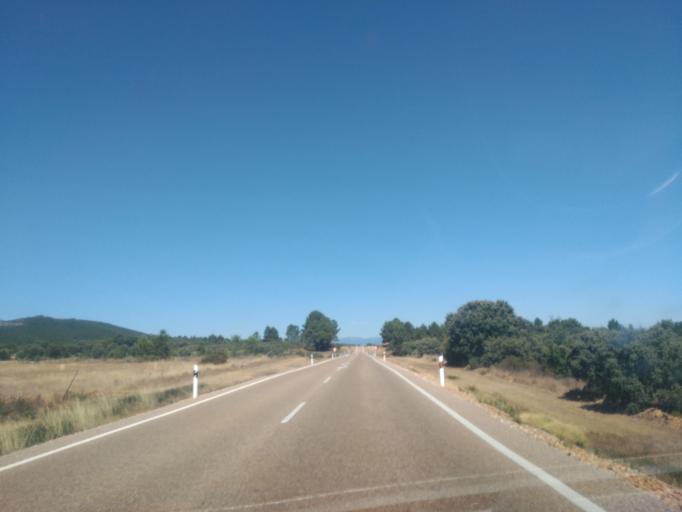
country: ES
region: Castille and Leon
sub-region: Provincia de Zamora
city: Ferreras de Abajo
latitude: 41.9159
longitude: -6.0864
